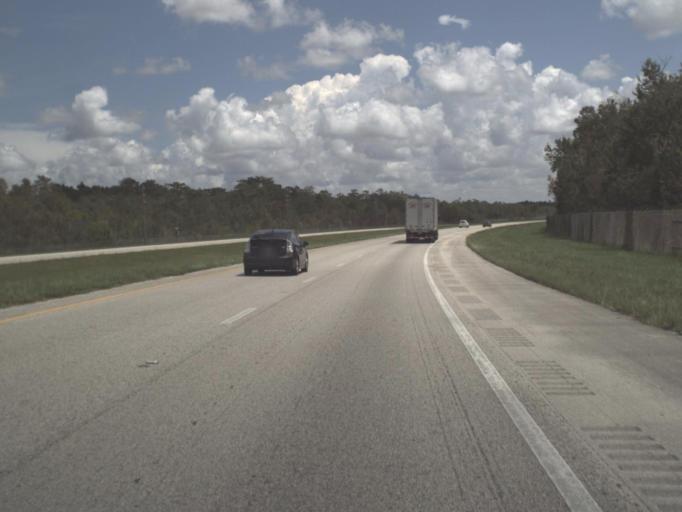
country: US
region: Florida
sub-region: Collier County
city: Immokalee
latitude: 26.1654
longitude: -81.2439
